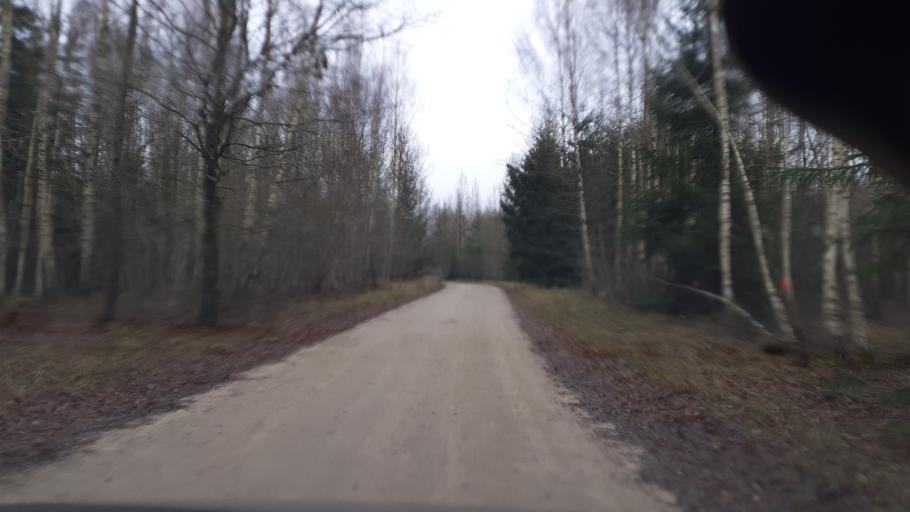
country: LV
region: Kuldigas Rajons
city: Kuldiga
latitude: 57.0292
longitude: 21.8702
